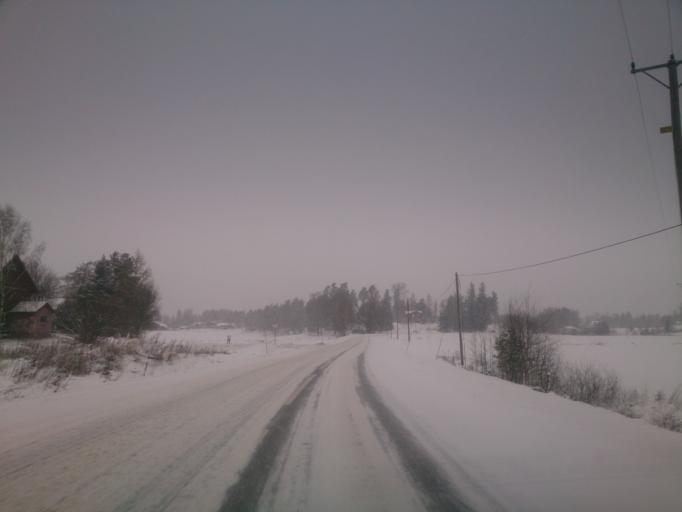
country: SE
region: OEstergoetland
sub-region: Finspangs Kommun
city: Finspang
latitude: 58.6717
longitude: 15.7554
